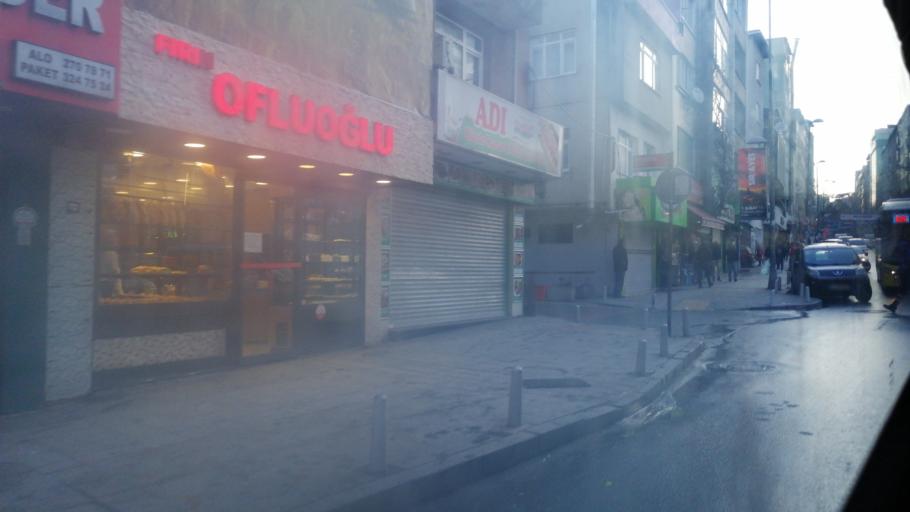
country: TR
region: Istanbul
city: Sisli
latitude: 41.0791
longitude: 28.9963
